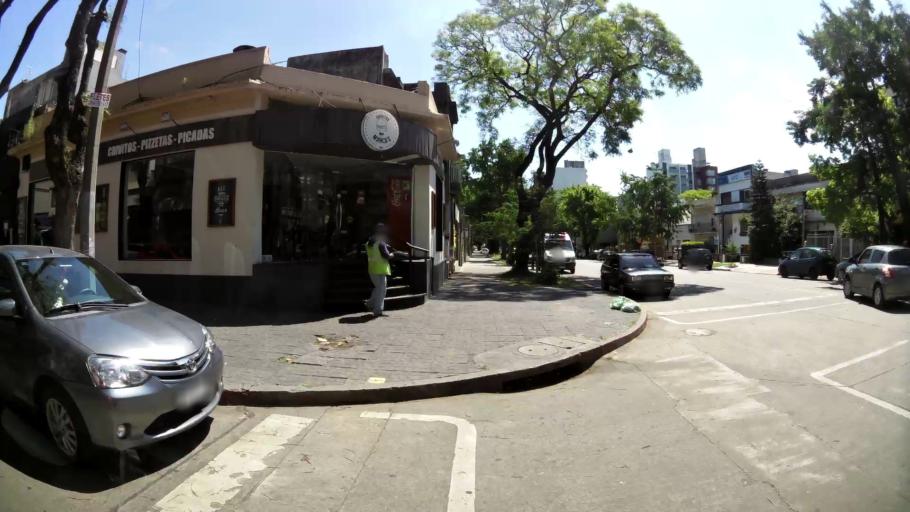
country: UY
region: Montevideo
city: Montevideo
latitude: -34.9144
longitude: -56.1563
